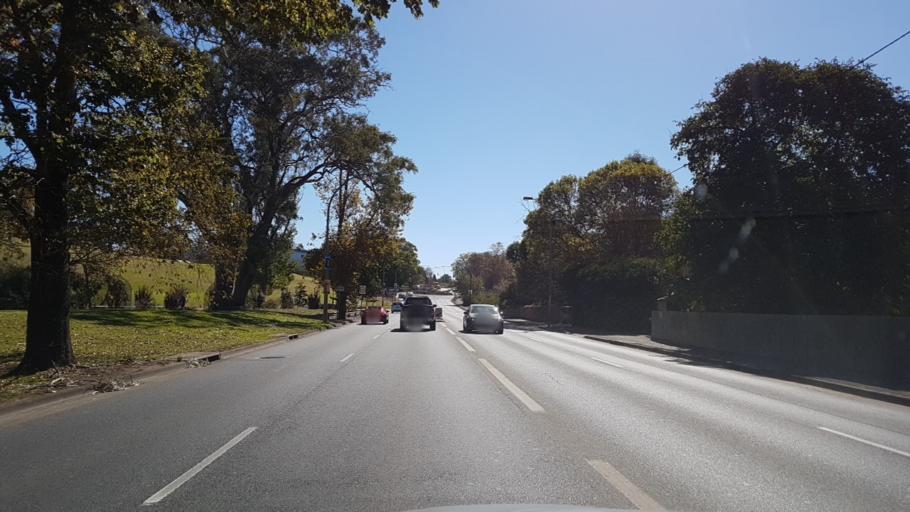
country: AU
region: South Australia
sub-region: Mount Barker
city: Mount Barker
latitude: -35.0711
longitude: 138.8572
